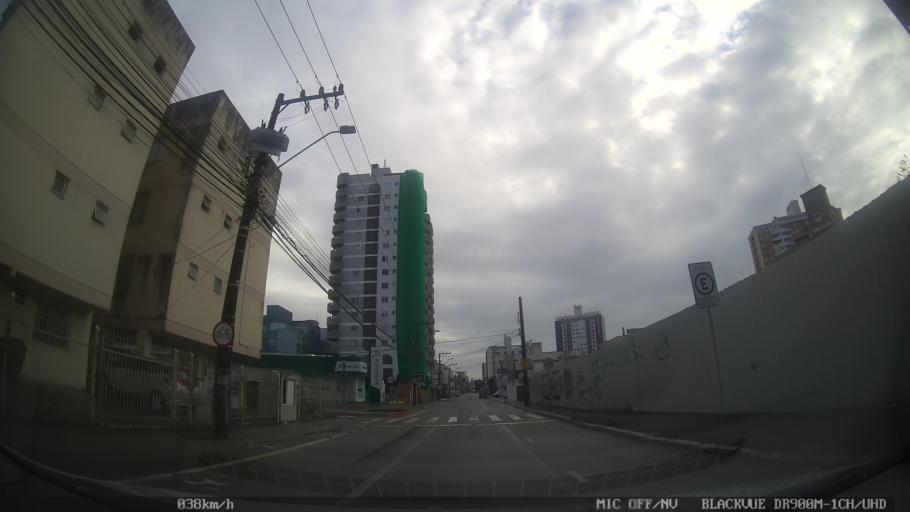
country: BR
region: Santa Catarina
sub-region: Sao Jose
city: Campinas
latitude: -27.5959
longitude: -48.6133
